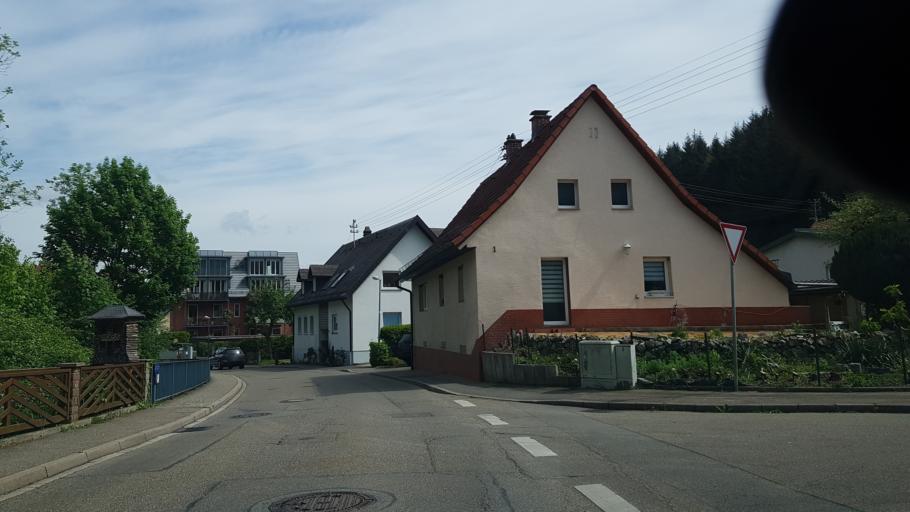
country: DE
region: Baden-Wuerttemberg
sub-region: Freiburg Region
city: Kirchzarten
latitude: 47.9657
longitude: 7.9087
